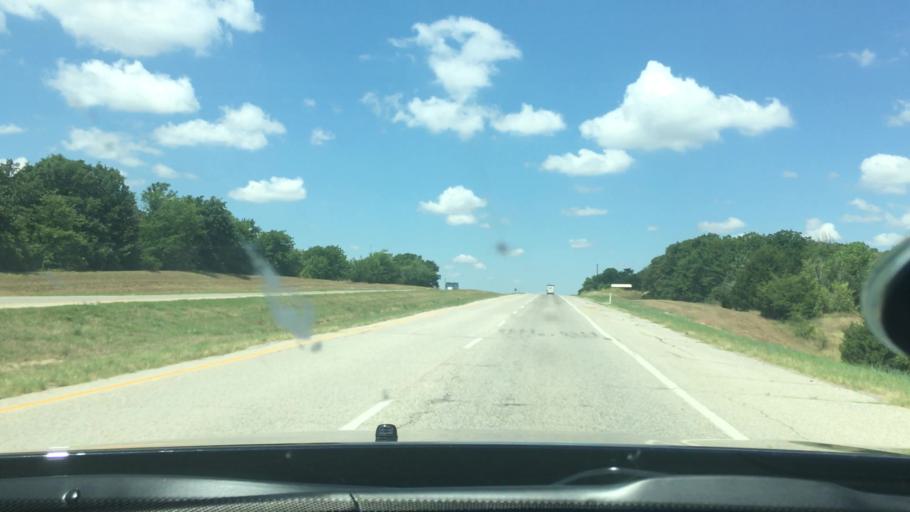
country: US
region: Oklahoma
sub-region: Carter County
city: Wilson
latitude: 34.1730
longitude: -97.3829
